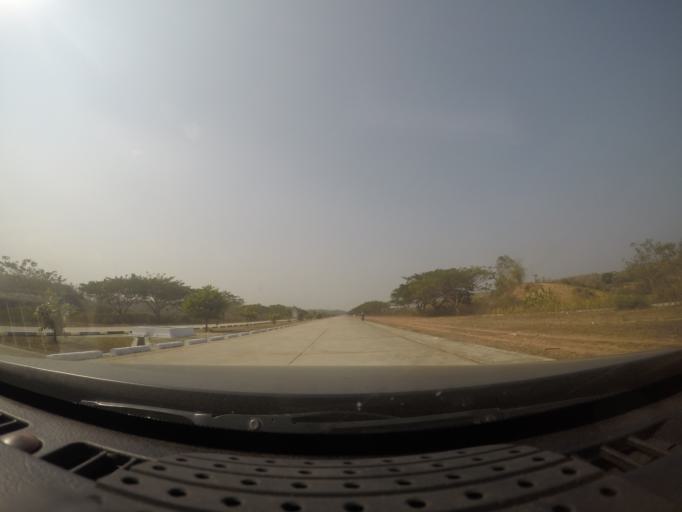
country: MM
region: Mandalay
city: Nay Pyi Taw
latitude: 20.0272
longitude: 95.9433
